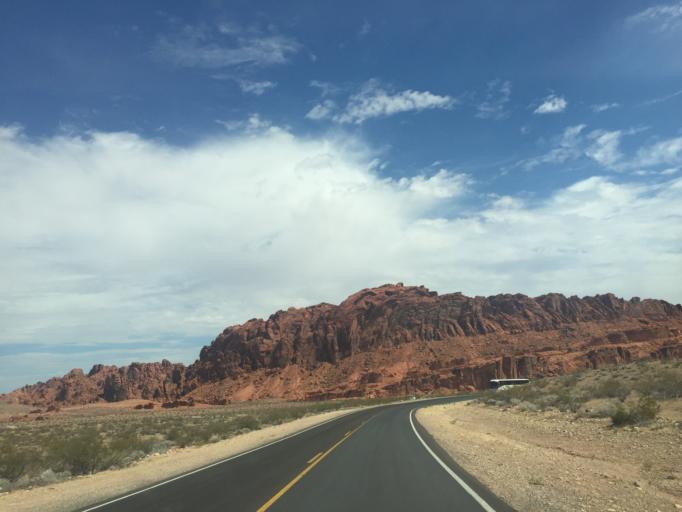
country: US
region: Nevada
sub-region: Clark County
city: Moapa Valley
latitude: 36.4251
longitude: -114.5417
